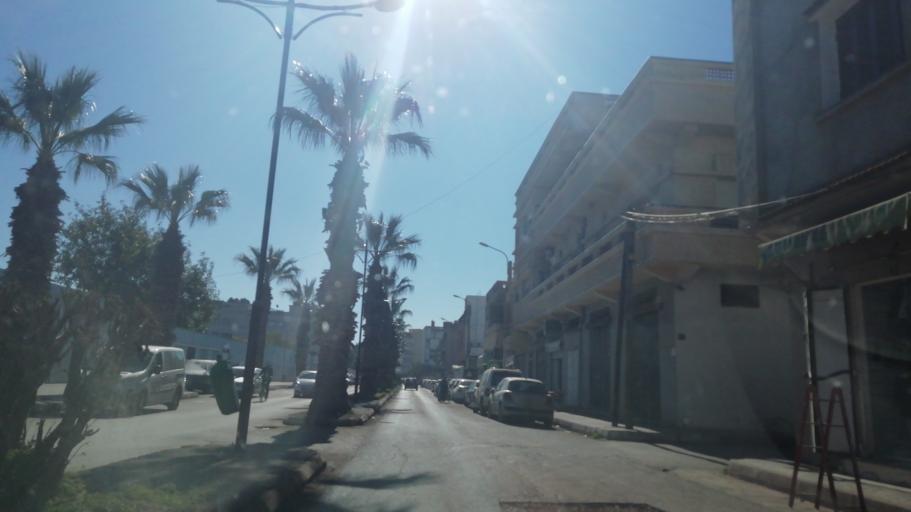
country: DZ
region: Oran
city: Es Senia
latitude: 35.6520
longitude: -0.6221
